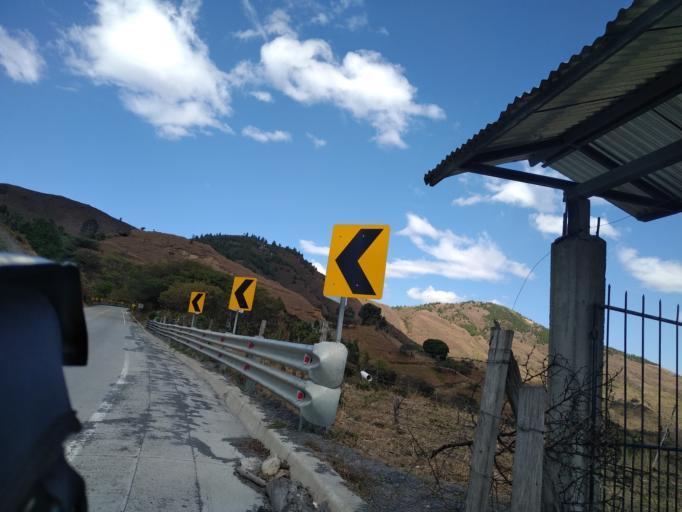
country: EC
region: Loja
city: Loja
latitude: -4.3453
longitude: -79.1882
